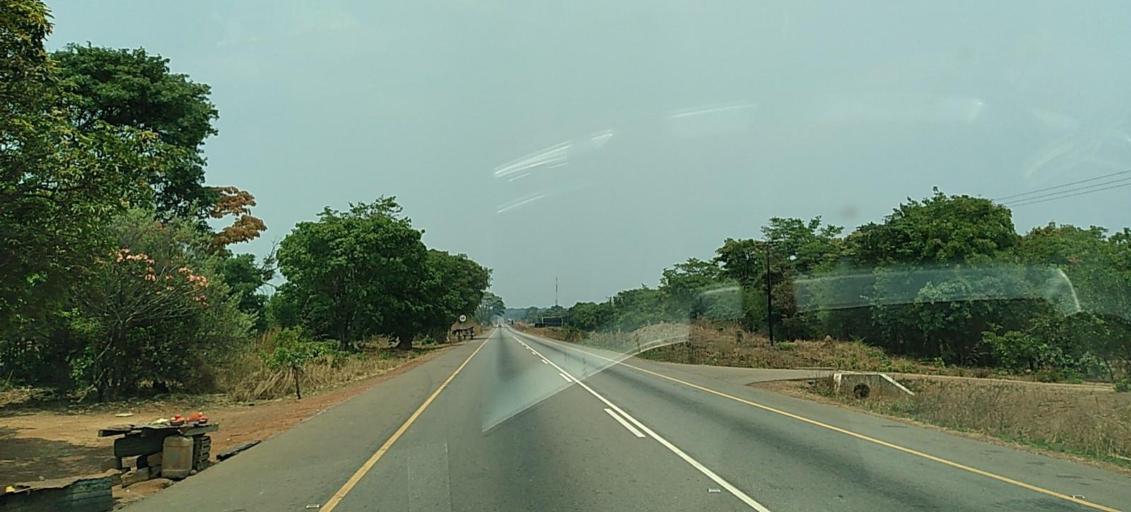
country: ZM
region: Copperbelt
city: Chingola
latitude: -12.5532
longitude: 27.7063
